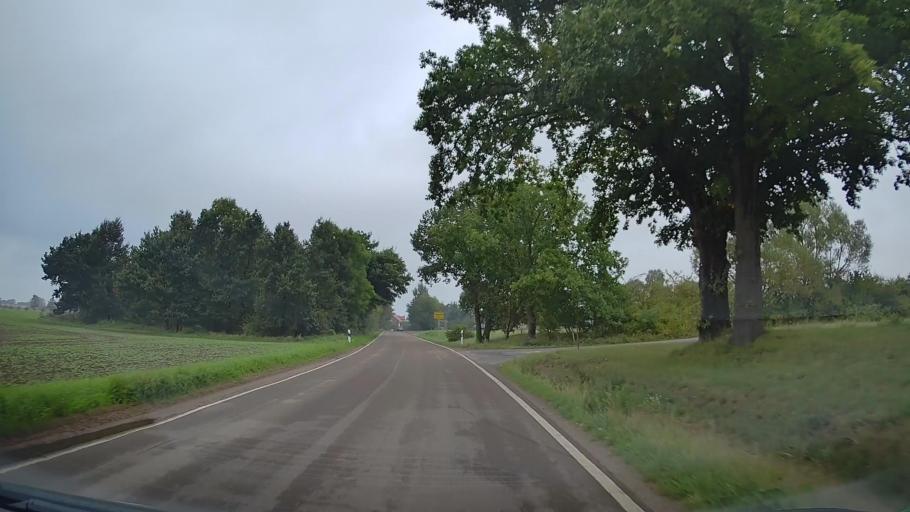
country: DE
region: Mecklenburg-Vorpommern
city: Blowatz
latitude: 53.9724
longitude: 11.5535
